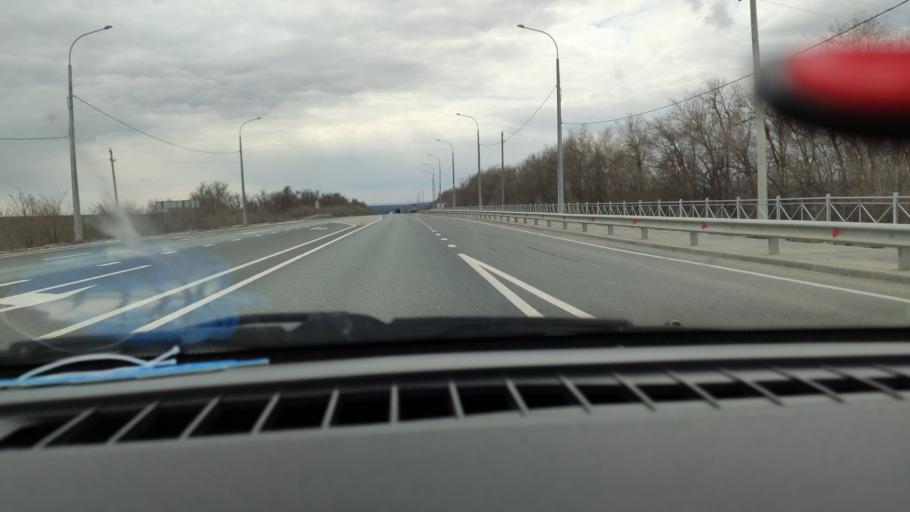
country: RU
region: Saratov
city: Yelshanka
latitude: 51.8893
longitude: 46.5215
